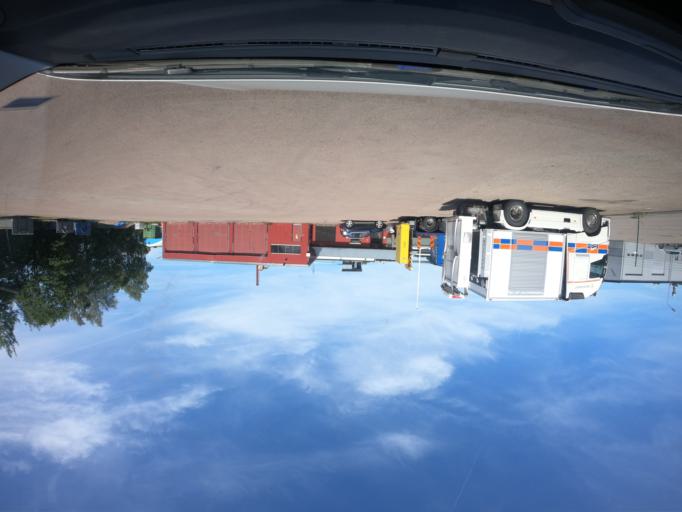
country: SE
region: Skane
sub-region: Orkelljunga Kommun
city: OErkelljunga
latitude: 56.2863
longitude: 13.3016
